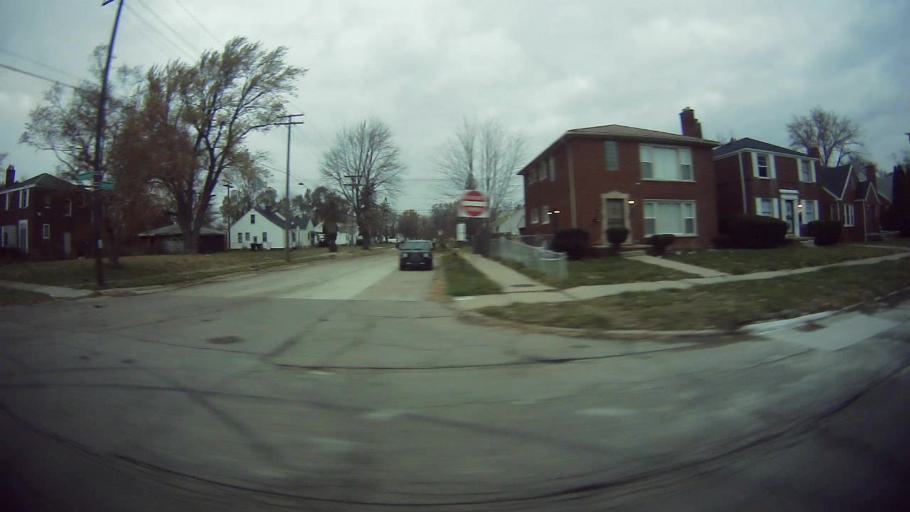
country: US
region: Michigan
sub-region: Macomb County
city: Warren
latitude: 42.4412
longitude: -83.0330
